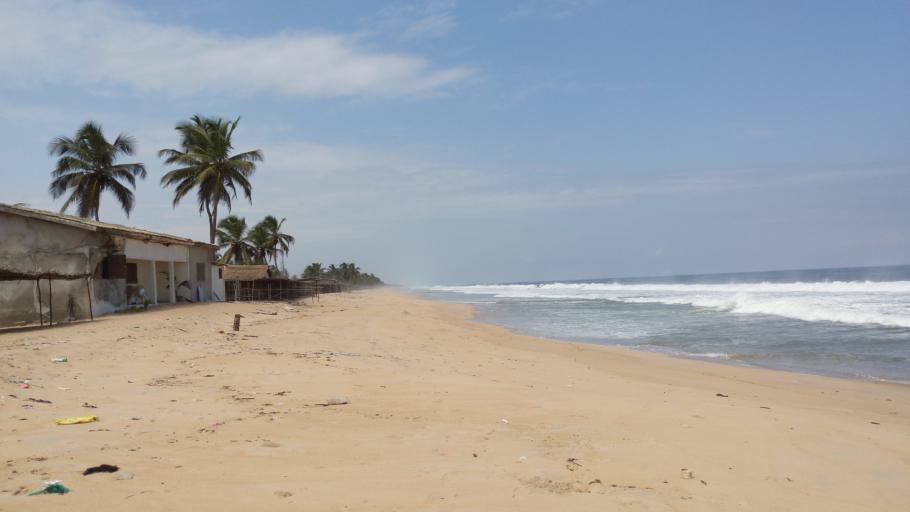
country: CI
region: Sud-Comoe
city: Grand-Bassam
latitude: 5.1867
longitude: -3.6880
